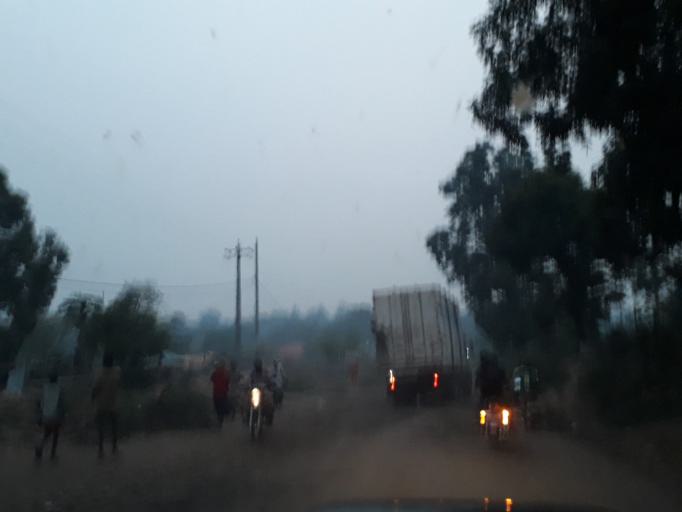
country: CD
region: Bandundu
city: Kikwit
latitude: -5.0396
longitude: 18.8349
